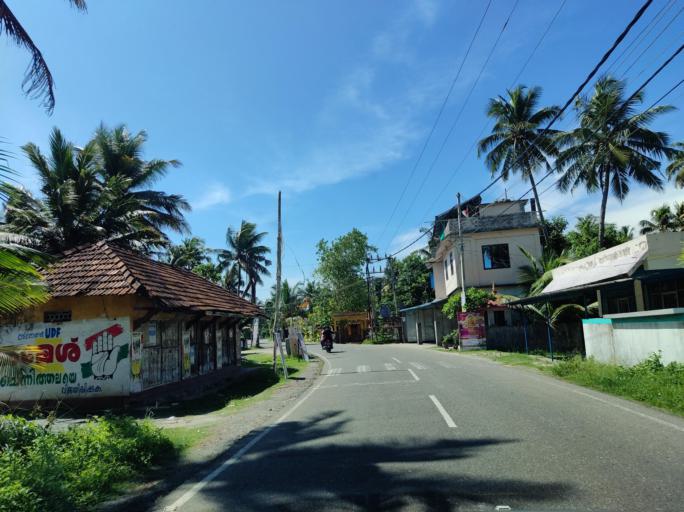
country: IN
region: Kerala
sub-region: Alappuzha
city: Kayankulam
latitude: 9.1836
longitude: 76.4422
